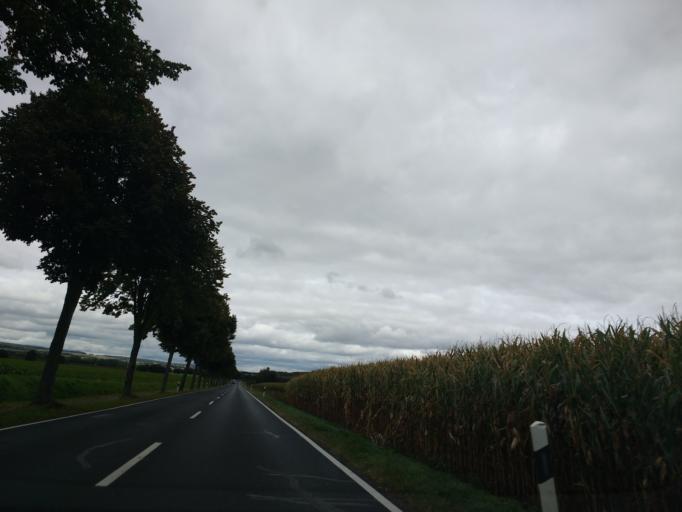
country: DE
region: Lower Saxony
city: Rosdorf
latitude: 51.4784
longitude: 9.9095
